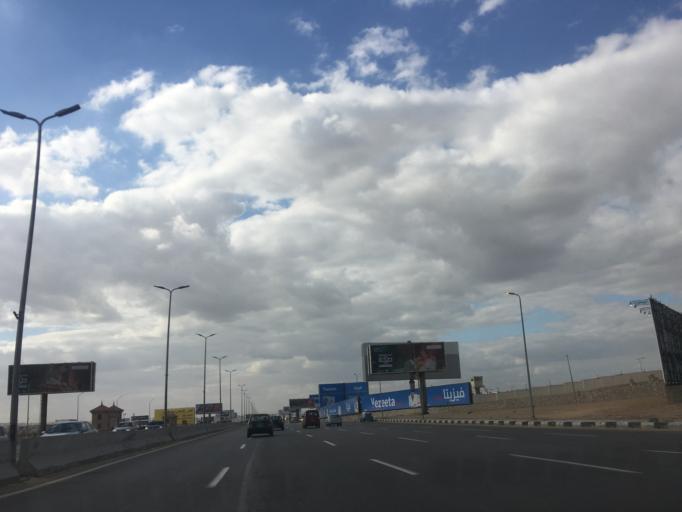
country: EG
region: Muhafazat al Qahirah
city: Cairo
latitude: 30.0231
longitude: 31.3681
